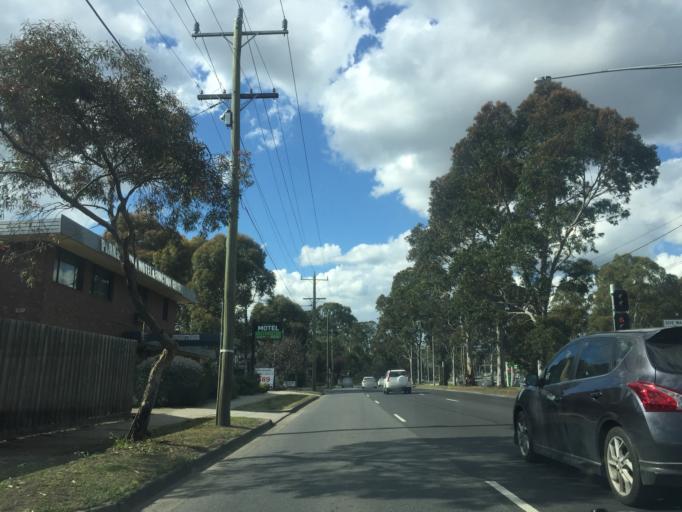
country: AU
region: Victoria
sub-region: Darebin
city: Kingsbury
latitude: -37.7146
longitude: 145.0443
